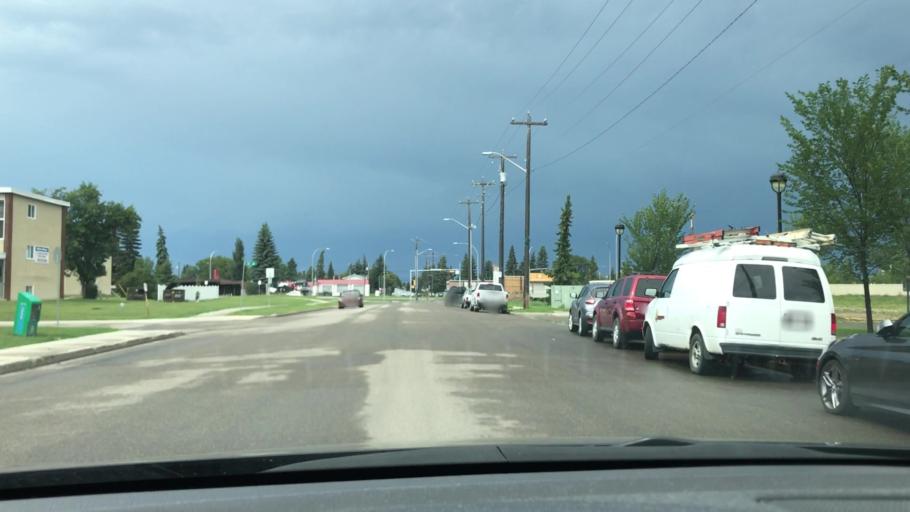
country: CA
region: Alberta
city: Edmonton
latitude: 53.5158
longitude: -113.4368
